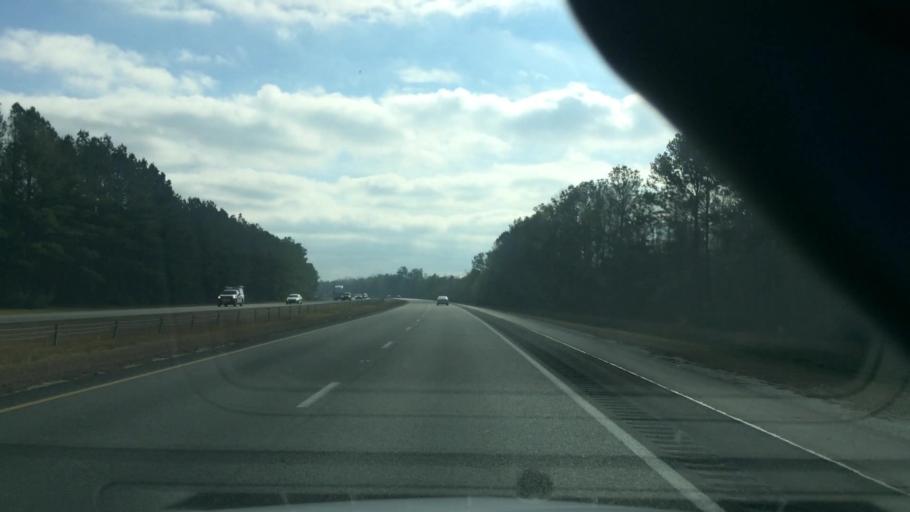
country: US
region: North Carolina
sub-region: Pender County
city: Rocky Point
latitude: 34.4672
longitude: -77.8802
